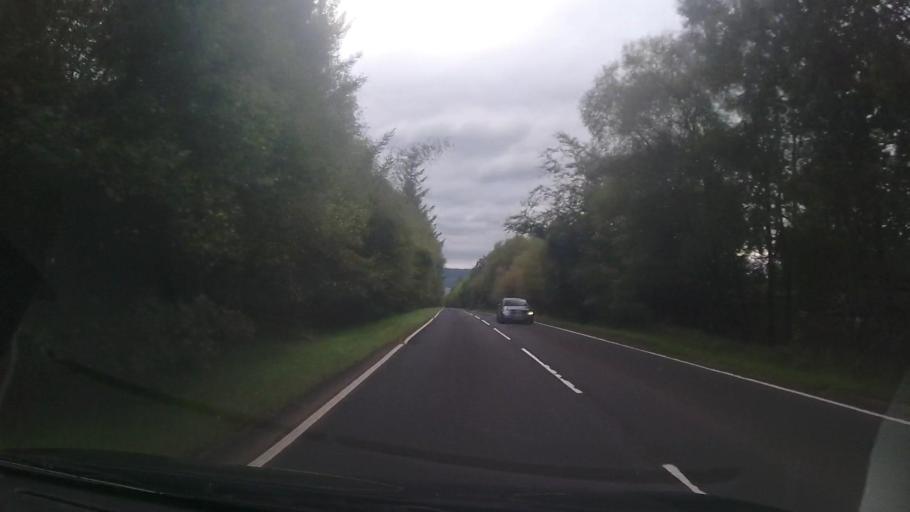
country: GB
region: Scotland
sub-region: Argyll and Bute
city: Garelochhead
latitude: 56.2290
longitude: -5.0057
